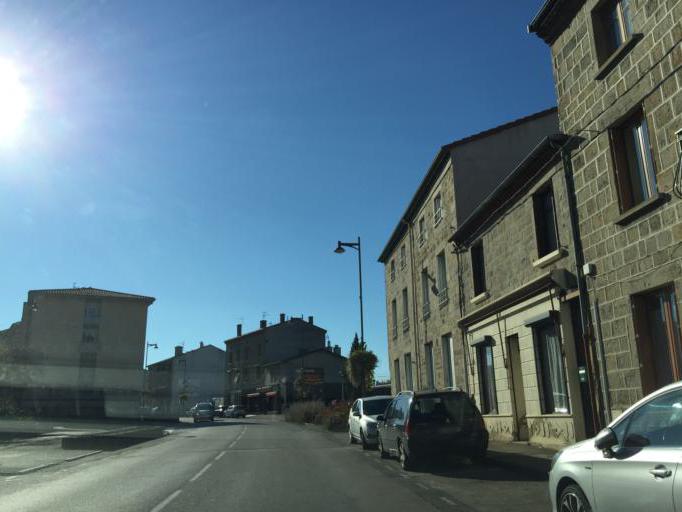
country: FR
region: Rhone-Alpes
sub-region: Departement de la Loire
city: Lorette
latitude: 45.5087
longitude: 4.5731
